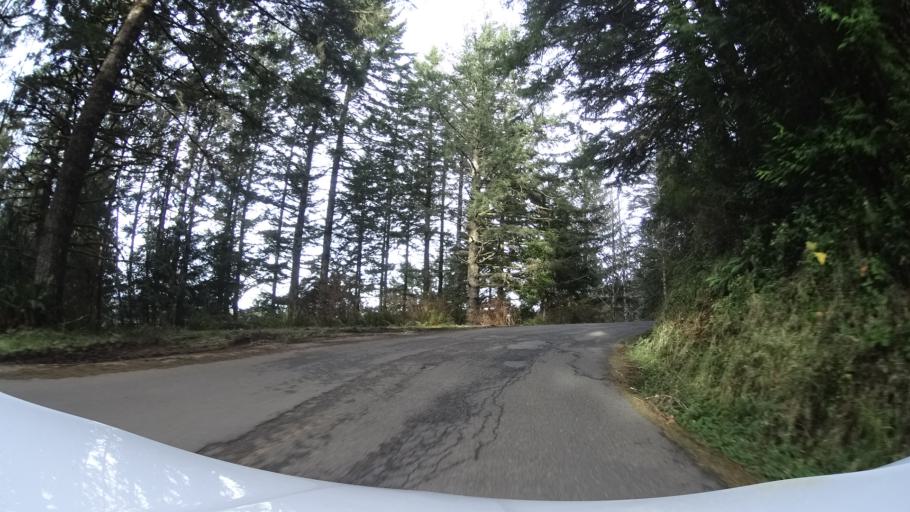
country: US
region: California
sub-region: Humboldt County
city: Ferndale
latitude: 40.5171
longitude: -124.2700
